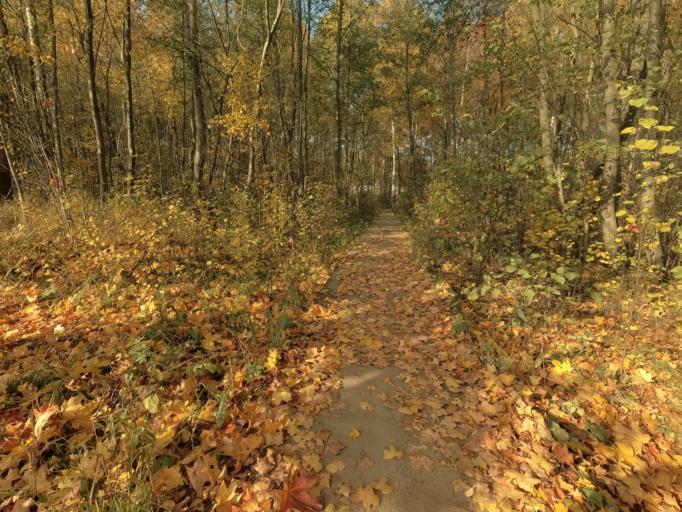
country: RU
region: Leningrad
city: Mga
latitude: 59.7586
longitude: 31.1149
